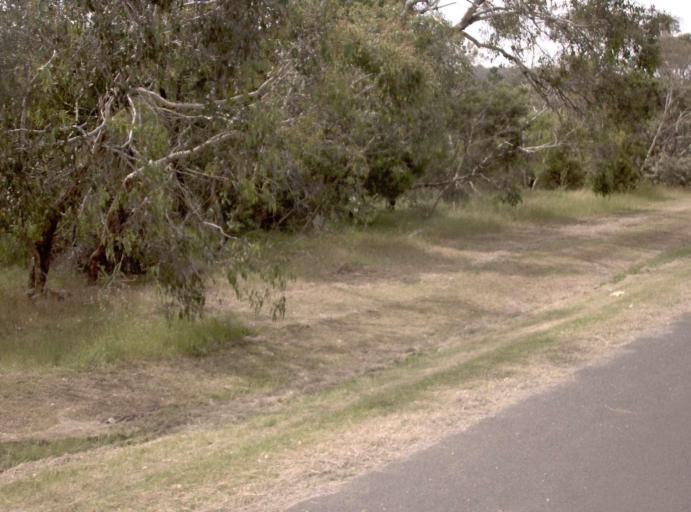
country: AU
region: Victoria
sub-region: Mornington Peninsula
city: Moorooduc
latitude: -38.2158
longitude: 145.1079
